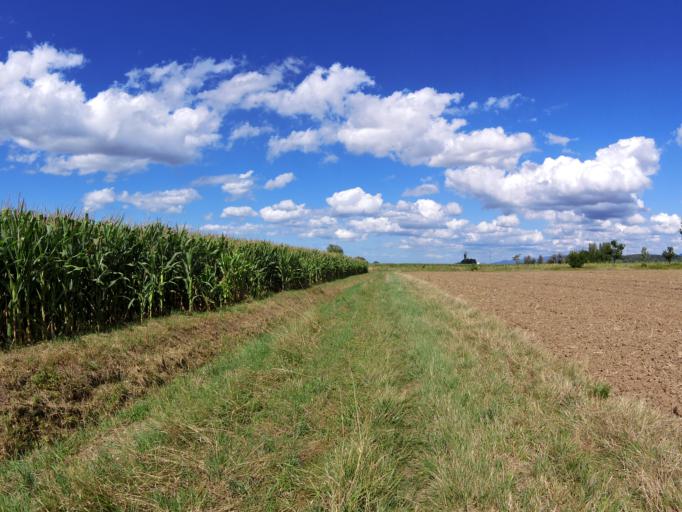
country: DE
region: Baden-Wuerttemberg
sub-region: Freiburg Region
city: Lahr
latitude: 48.3660
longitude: 7.8473
